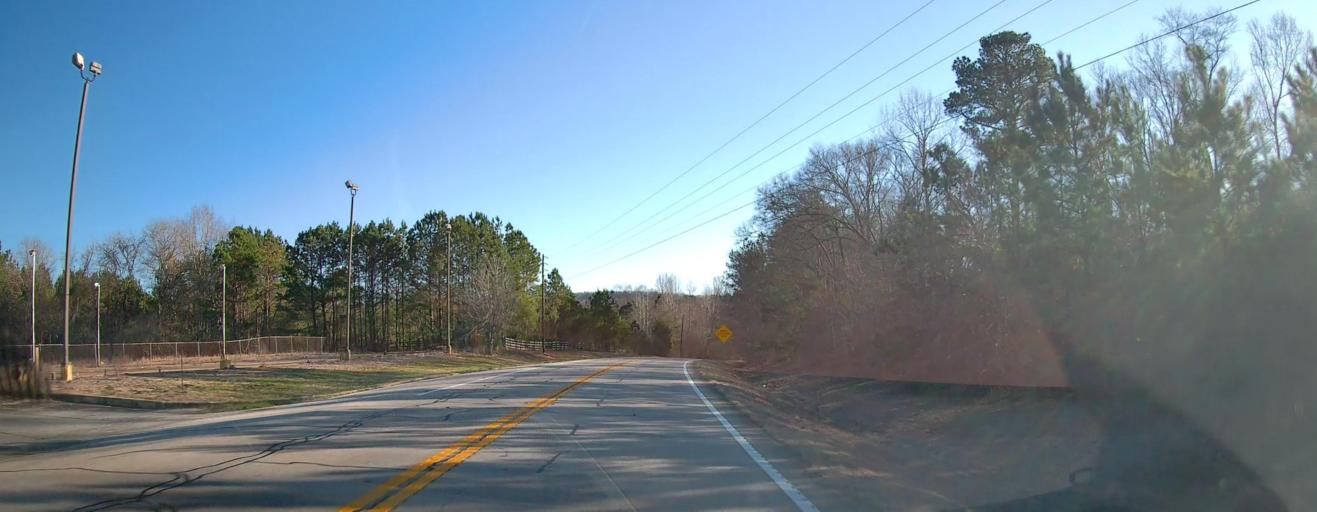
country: US
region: Georgia
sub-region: Meriwether County
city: Manchester
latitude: 32.8745
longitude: -84.5971
